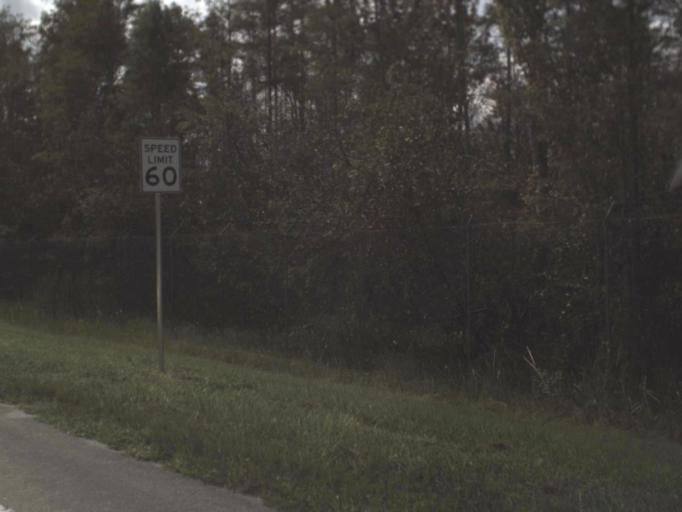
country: US
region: Florida
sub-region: Collier County
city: Orangetree
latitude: 26.0548
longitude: -81.3445
